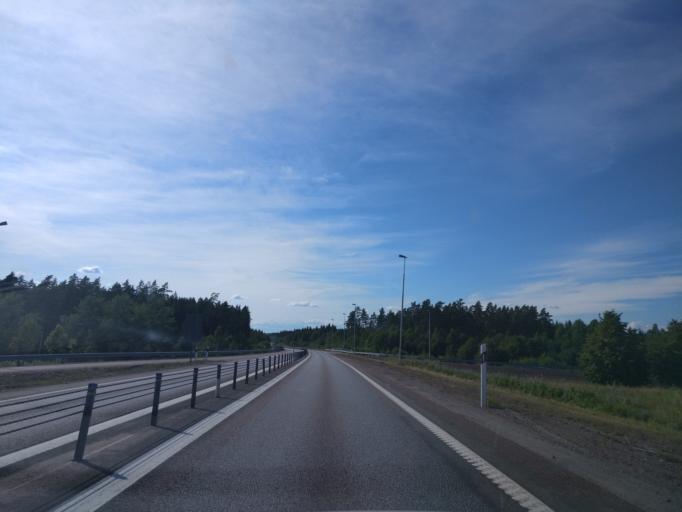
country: SE
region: Vaermland
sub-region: Kils Kommun
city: Kil
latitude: 59.4894
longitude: 13.3355
